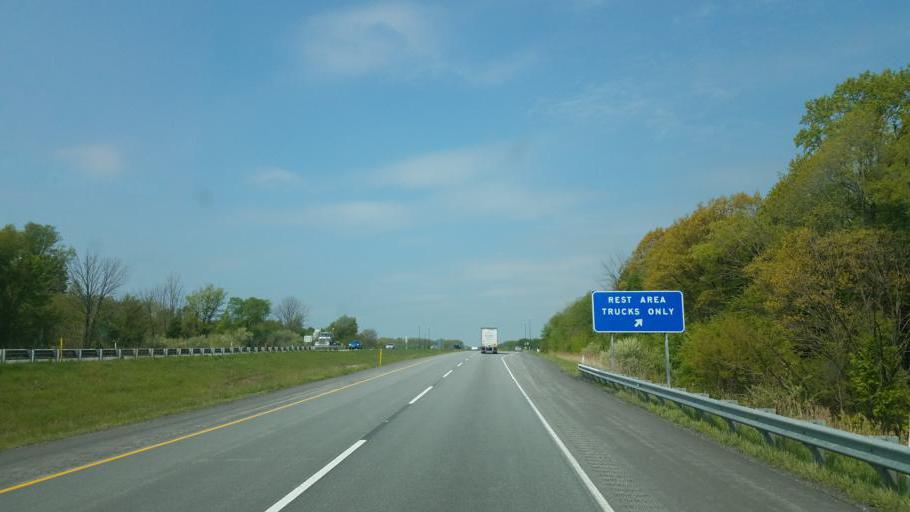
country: US
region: Indiana
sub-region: LaPorte County
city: Westville
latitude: 41.5882
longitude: -86.9143
